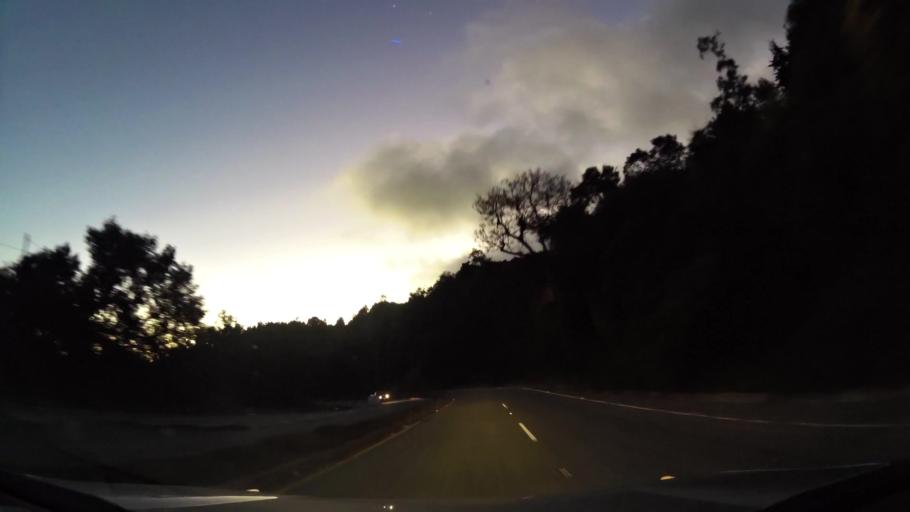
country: GT
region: Chimaltenango
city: Santa Apolonia
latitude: 14.7959
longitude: -90.9756
